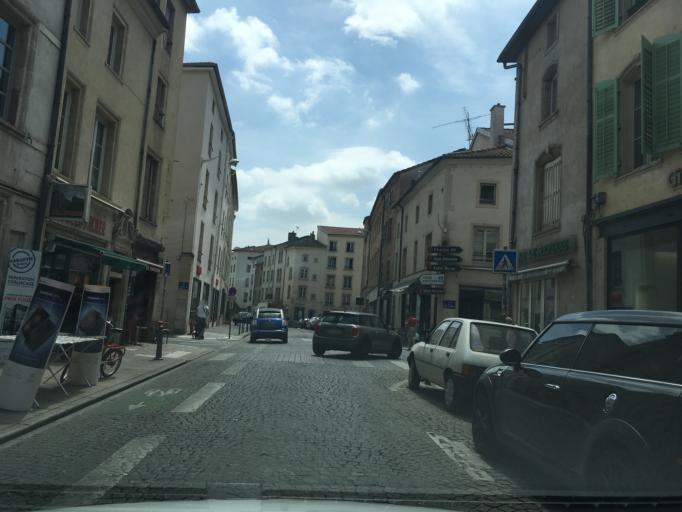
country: FR
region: Lorraine
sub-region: Departement de Meurthe-et-Moselle
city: Nancy
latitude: 48.6891
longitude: 6.1854
